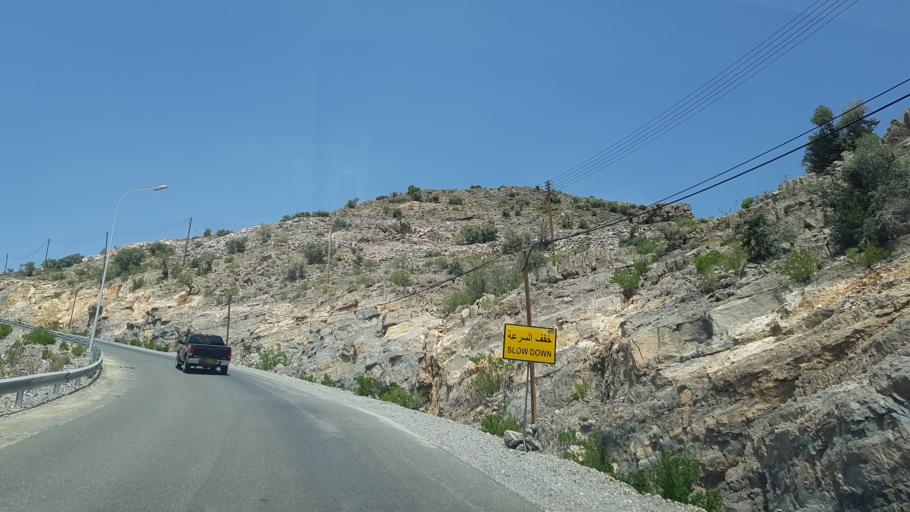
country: OM
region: Muhafazat ad Dakhiliyah
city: Izki
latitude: 23.0923
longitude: 57.6827
